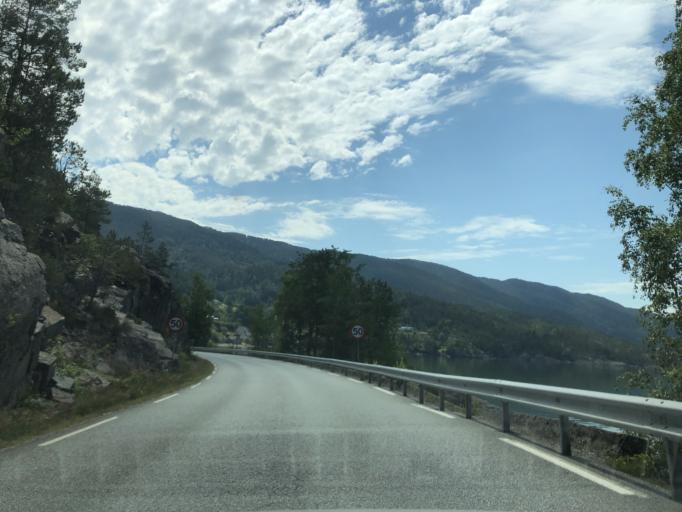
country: NO
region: Hordaland
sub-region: Jondal
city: Jondal
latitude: 60.3201
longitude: 6.3234
